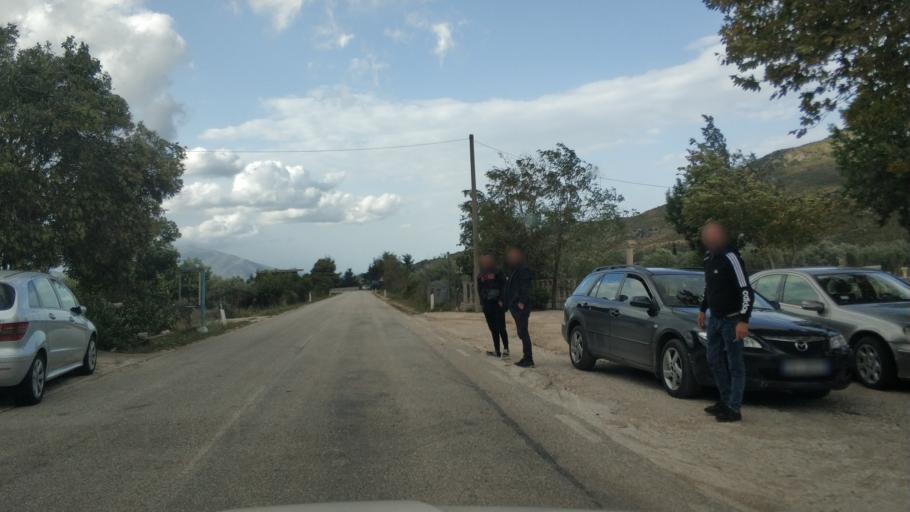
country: AL
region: Vlore
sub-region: Rrethi i Vlores
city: Orikum
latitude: 40.2705
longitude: 19.5136
